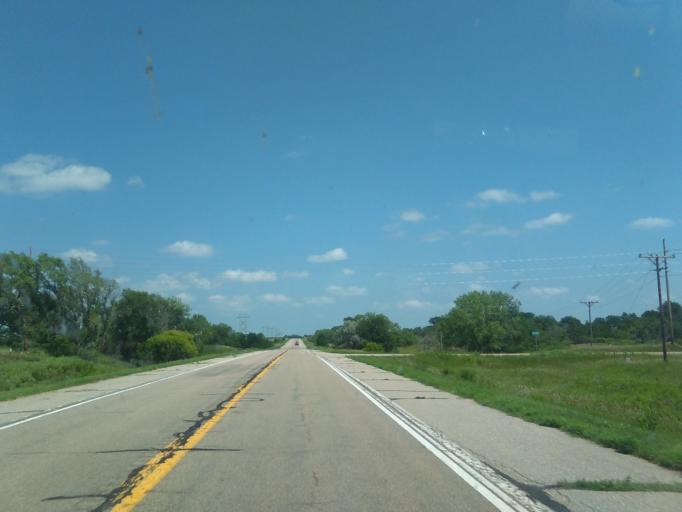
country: US
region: Nebraska
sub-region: Gosper County
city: Elwood
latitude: 40.6846
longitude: -99.8143
